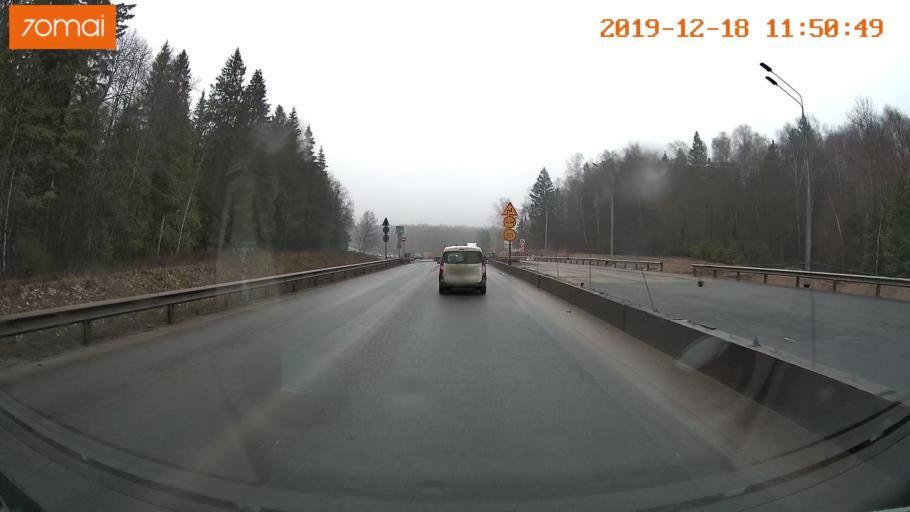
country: RU
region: Moskovskaya
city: Yershovo
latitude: 55.7886
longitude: 36.9211
